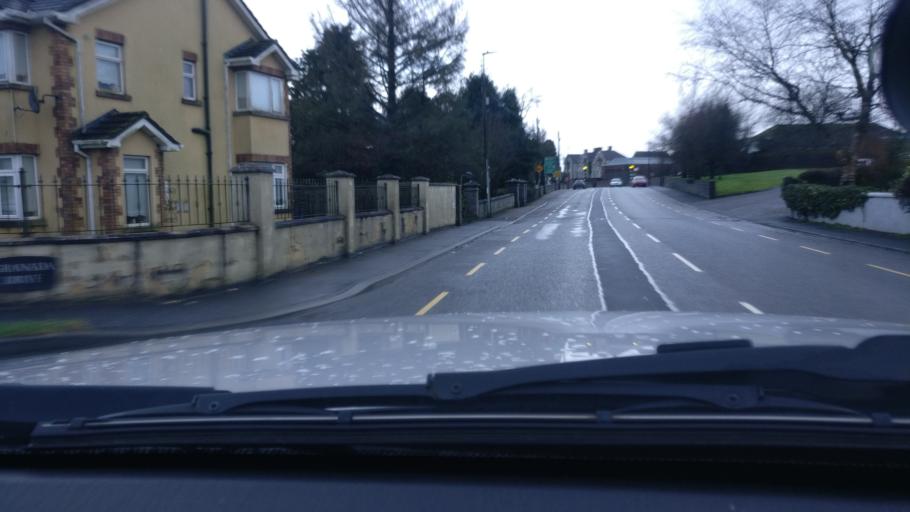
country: IE
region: Leinster
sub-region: An Longfort
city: Granard
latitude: 53.7798
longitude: -7.4854
